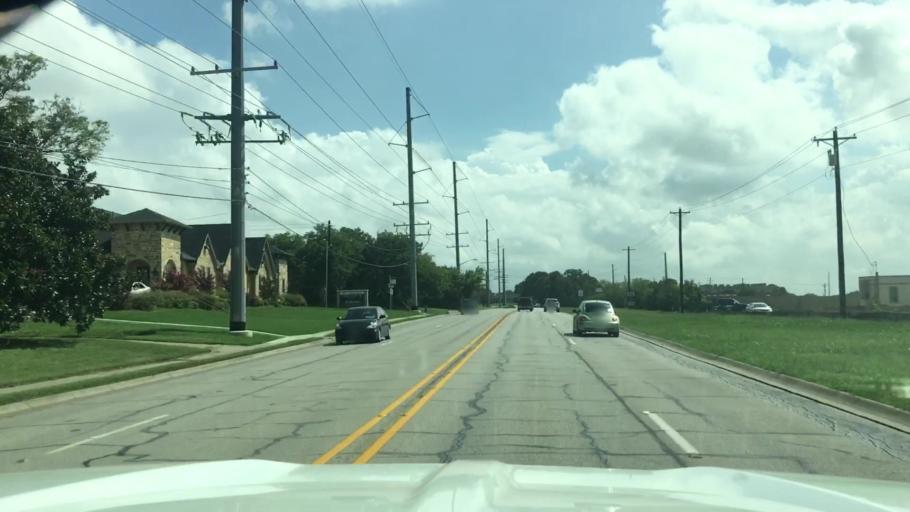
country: US
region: Texas
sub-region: Denton County
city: Denton
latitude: 33.2226
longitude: -97.1612
